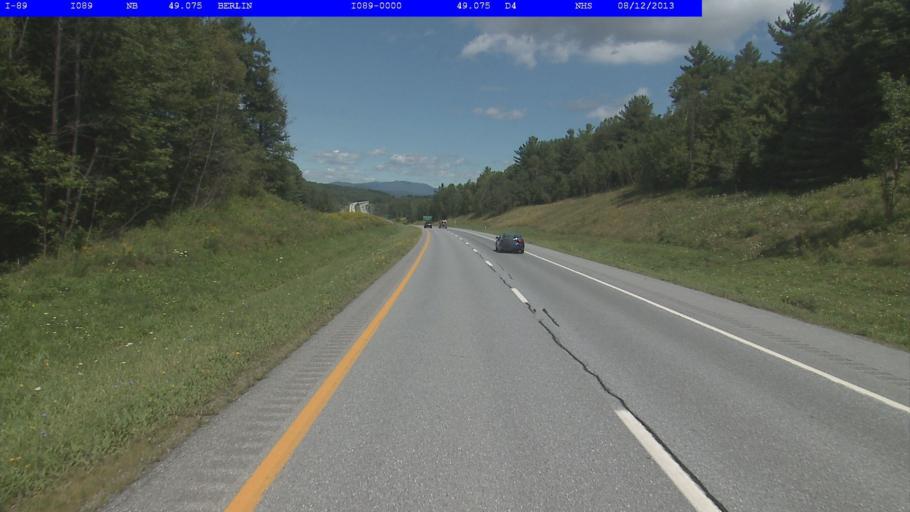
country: US
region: Vermont
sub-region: Washington County
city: Montpelier
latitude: 44.1987
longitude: -72.5770
